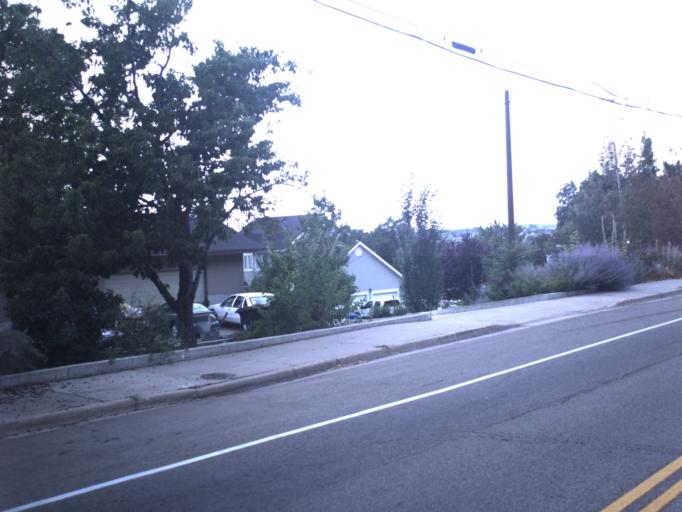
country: US
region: Utah
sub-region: Davis County
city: Farmington
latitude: 40.9497
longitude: -111.8827
